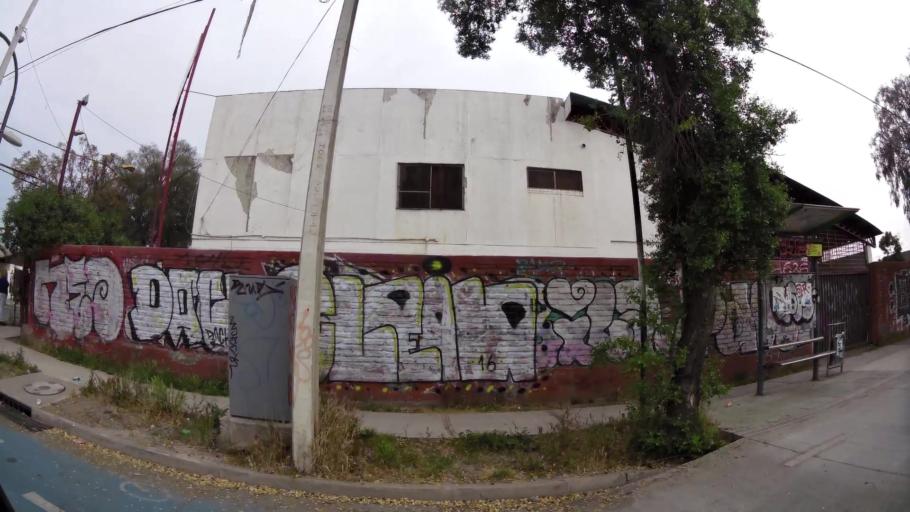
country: CL
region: Santiago Metropolitan
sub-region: Provincia de Santiago
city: Lo Prado
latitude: -33.5214
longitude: -70.7711
